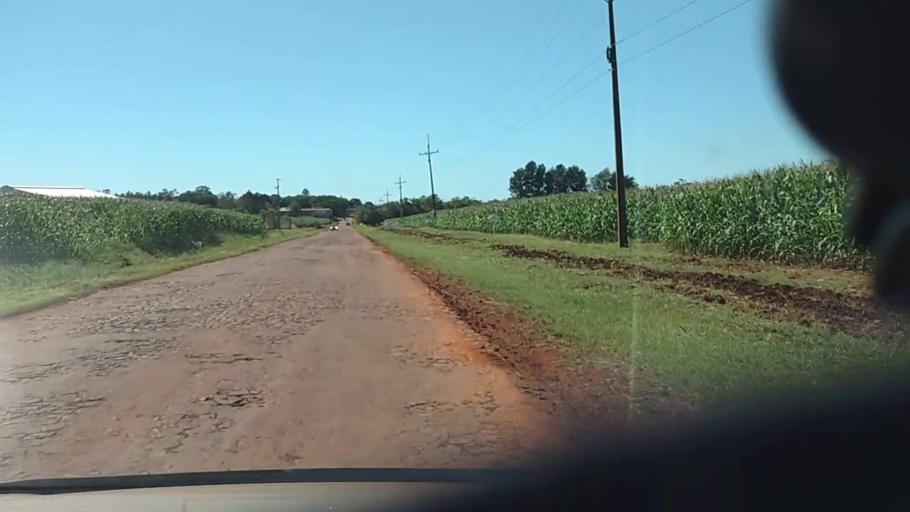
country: PY
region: Alto Parana
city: Naranjal
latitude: -25.9536
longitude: -55.1312
